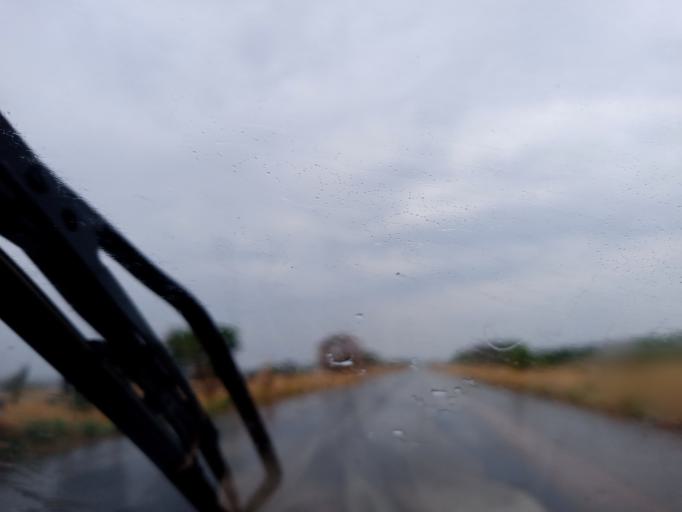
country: BR
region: Minas Gerais
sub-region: Ituiutaba
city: Ituiutaba
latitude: -19.0894
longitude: -49.5098
